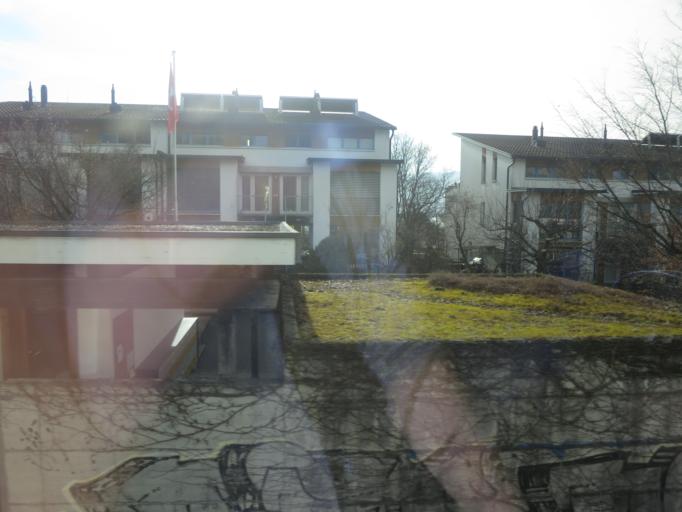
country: CH
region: Zurich
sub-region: Bezirk Meilen
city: Dorf
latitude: 47.2357
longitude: 8.7478
